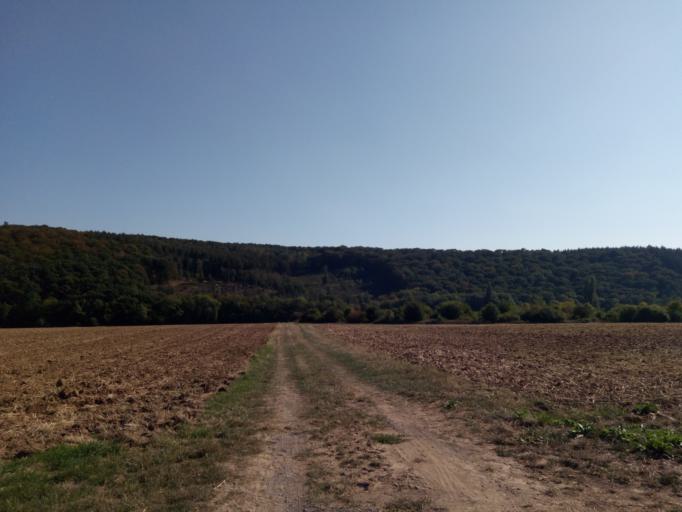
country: DE
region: Rheinland-Pfalz
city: Waldlaubersheim
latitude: 49.9206
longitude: 7.8277
